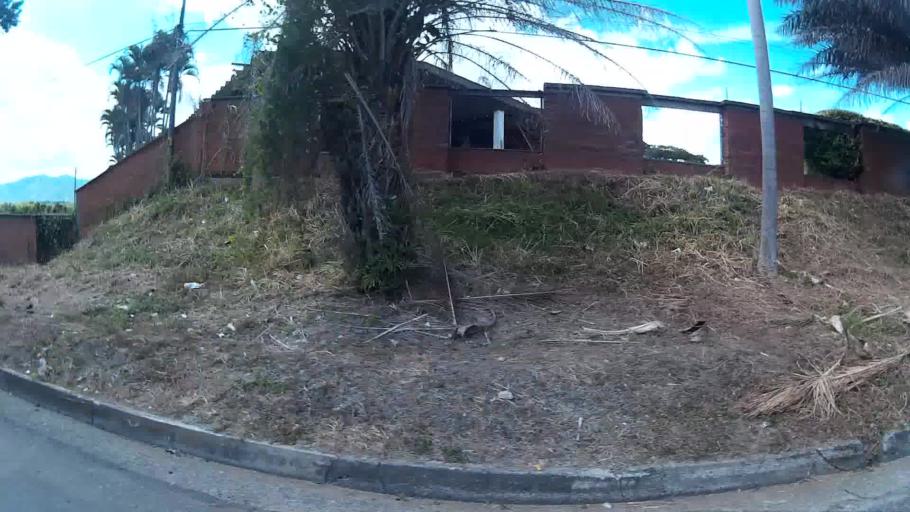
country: CO
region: Valle del Cauca
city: Cartago
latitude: 4.8087
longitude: -75.8411
